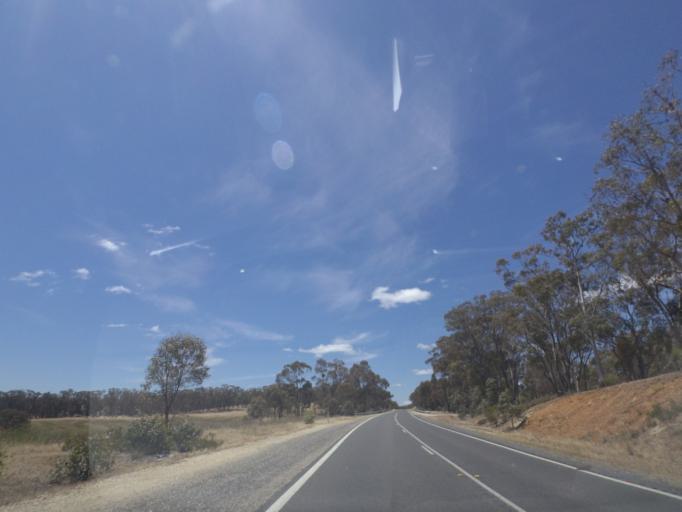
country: AU
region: Victoria
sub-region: Mount Alexander
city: Castlemaine
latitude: -37.1658
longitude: 144.1492
